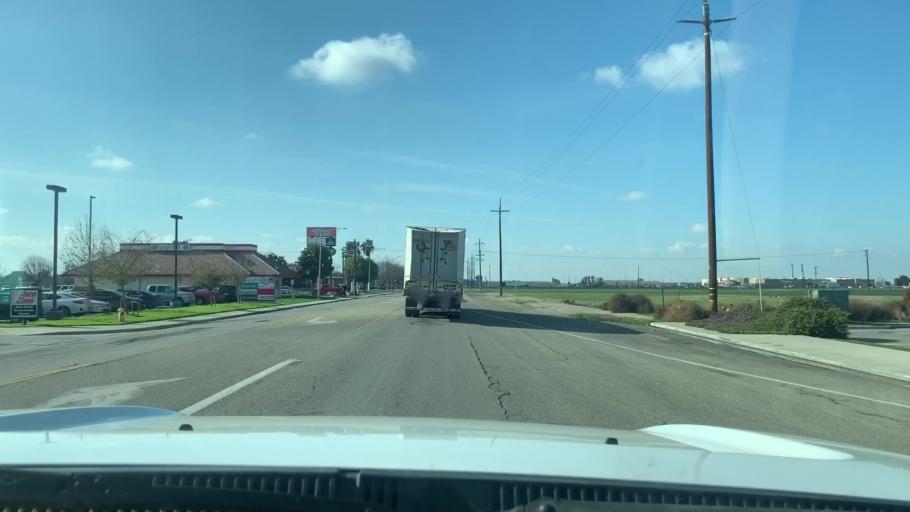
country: US
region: California
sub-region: Kern County
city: Wasco
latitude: 35.6016
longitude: -119.3506
